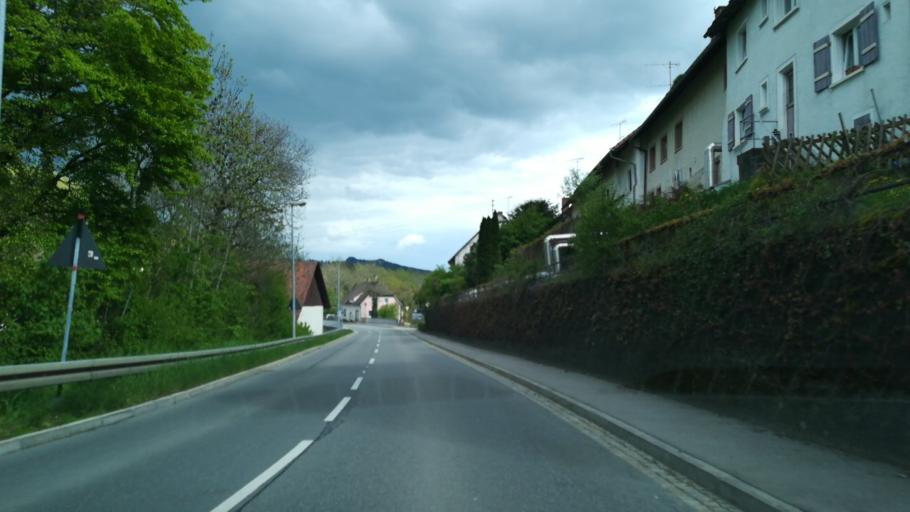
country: DE
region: Baden-Wuerttemberg
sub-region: Freiburg Region
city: Tengen
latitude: 47.8144
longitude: 8.6820
